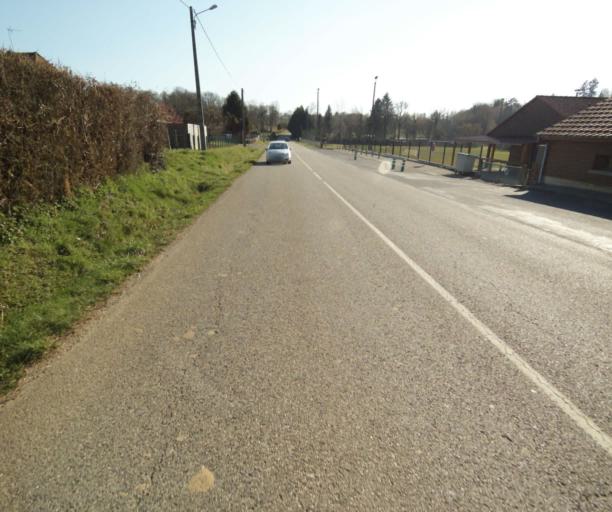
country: FR
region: Limousin
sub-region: Departement de la Correze
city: Saint-Clement
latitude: 45.3369
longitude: 1.6816
